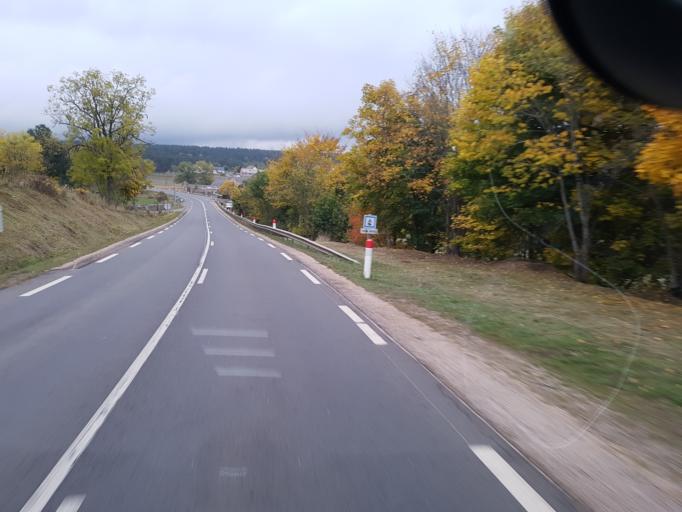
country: FR
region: Languedoc-Roussillon
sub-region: Departement de la Lozere
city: Mende
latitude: 44.5835
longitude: 3.6430
